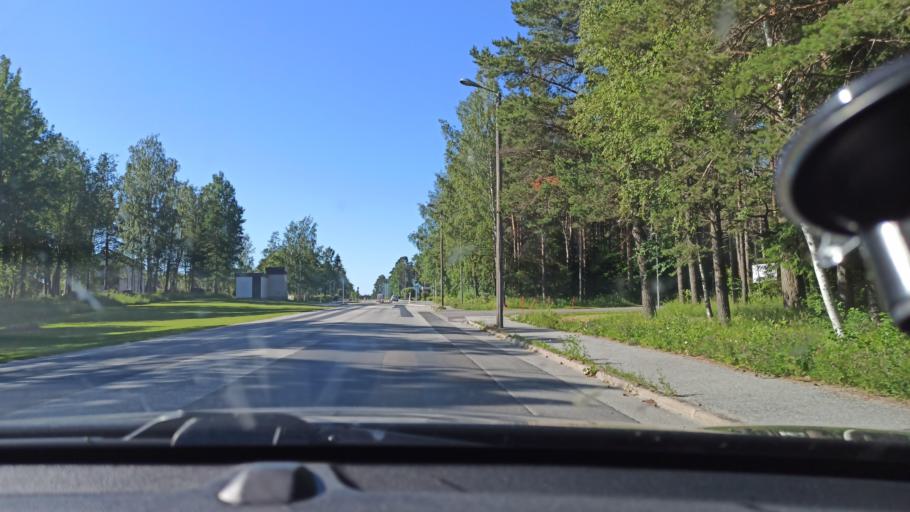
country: FI
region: Ostrobothnia
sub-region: Jakobstadsregionen
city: Jakobstad
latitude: 63.6797
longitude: 22.7181
